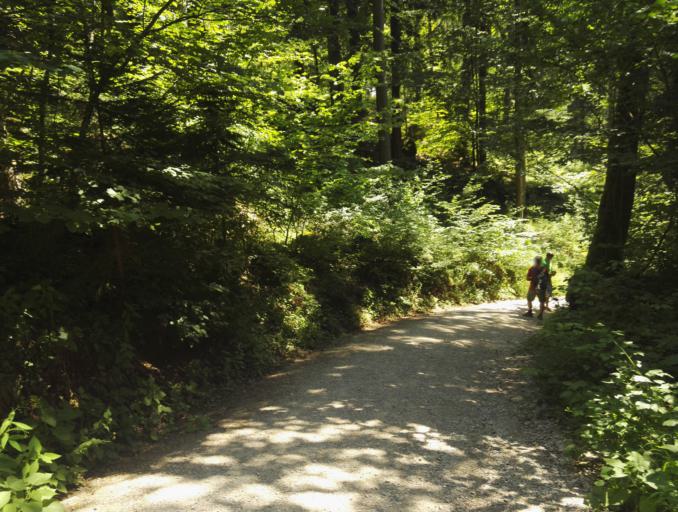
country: AT
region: Styria
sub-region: Politischer Bezirk Graz-Umgebung
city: Rothelstein
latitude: 47.3414
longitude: 15.3901
